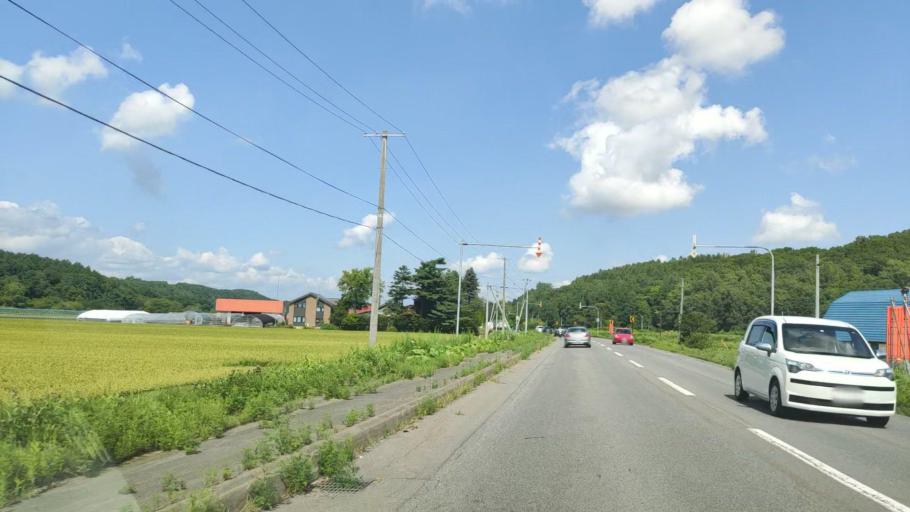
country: JP
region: Hokkaido
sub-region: Asahikawa-shi
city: Asahikawa
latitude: 43.6272
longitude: 142.4652
